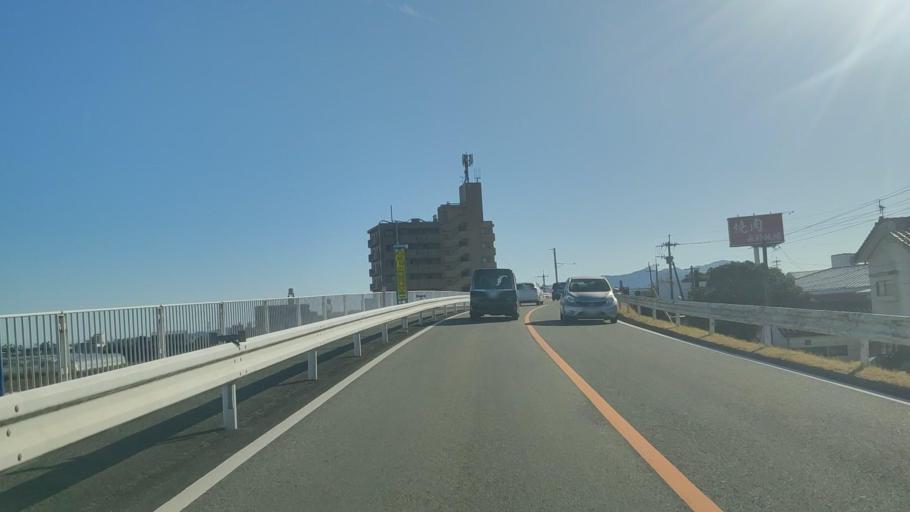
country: JP
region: Miyazaki
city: Miyazaki-shi
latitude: 31.8836
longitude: 131.4287
